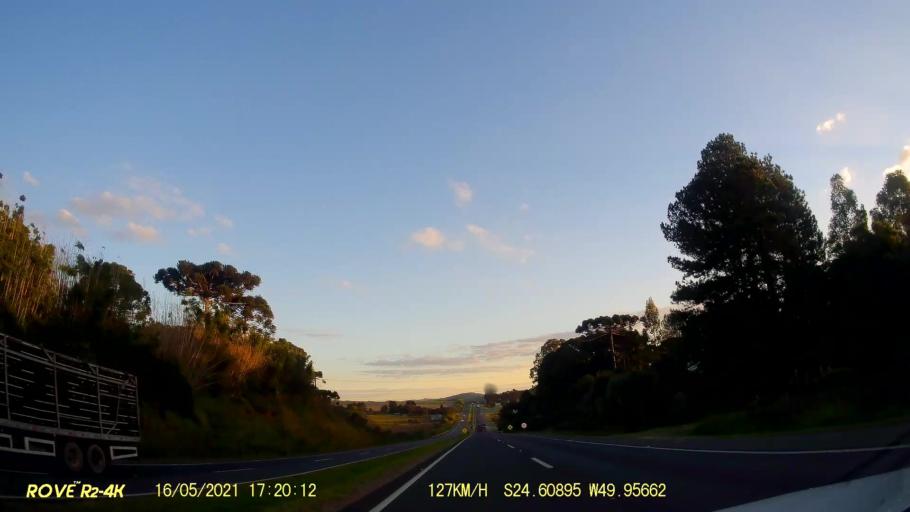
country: BR
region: Parana
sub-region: Pirai Do Sul
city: Pirai do Sul
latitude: -24.6093
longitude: -49.9567
